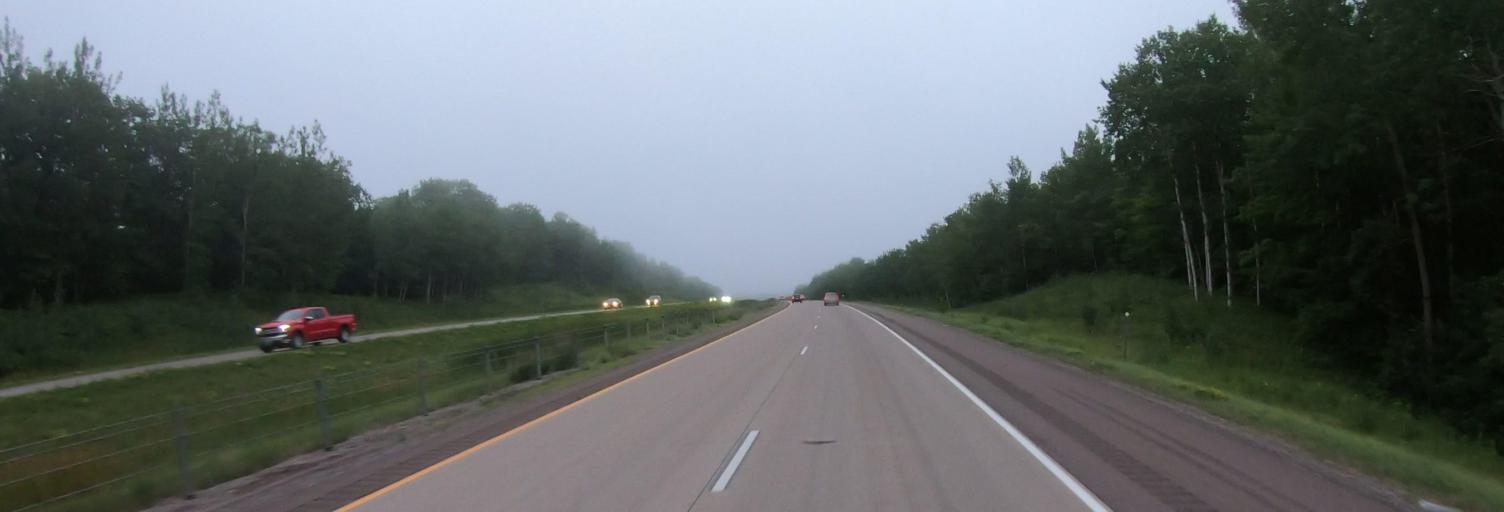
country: US
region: Minnesota
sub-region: Carlton County
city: Moose Lake
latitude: 46.4664
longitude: -92.7192
